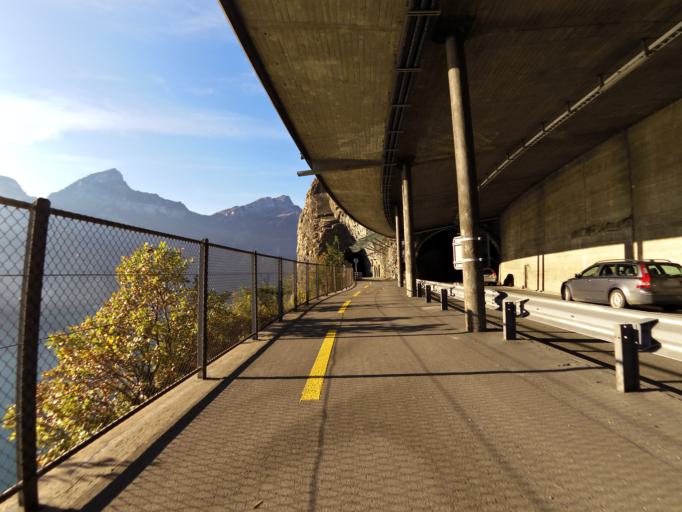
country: CH
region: Uri
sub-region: Uri
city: Flueelen
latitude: 46.9235
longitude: 8.6159
